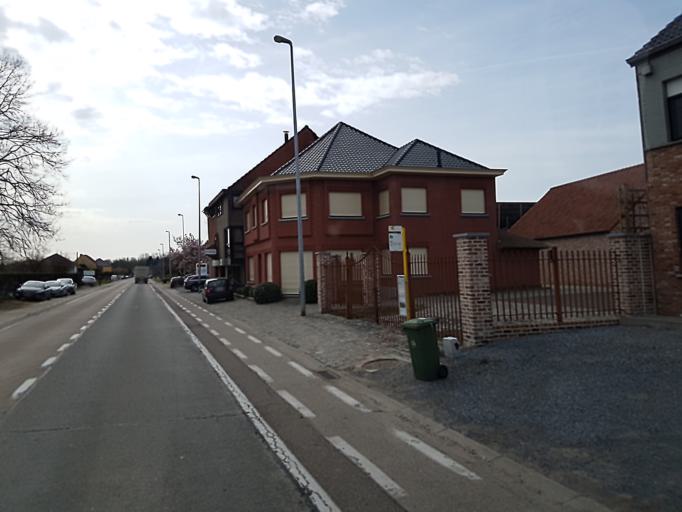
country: BE
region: Flanders
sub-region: Provincie Vlaams-Brabant
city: Scherpenheuvel-Zichem
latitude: 51.0217
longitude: 4.9883
